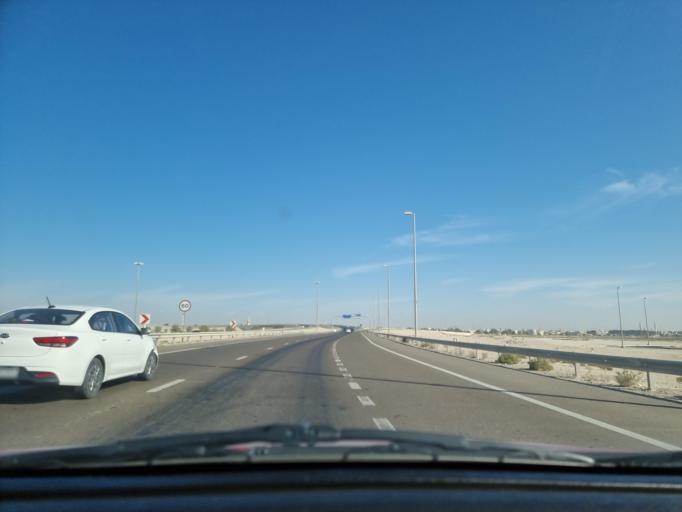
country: AE
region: Abu Dhabi
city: Abu Dhabi
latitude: 24.4102
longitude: 54.7160
